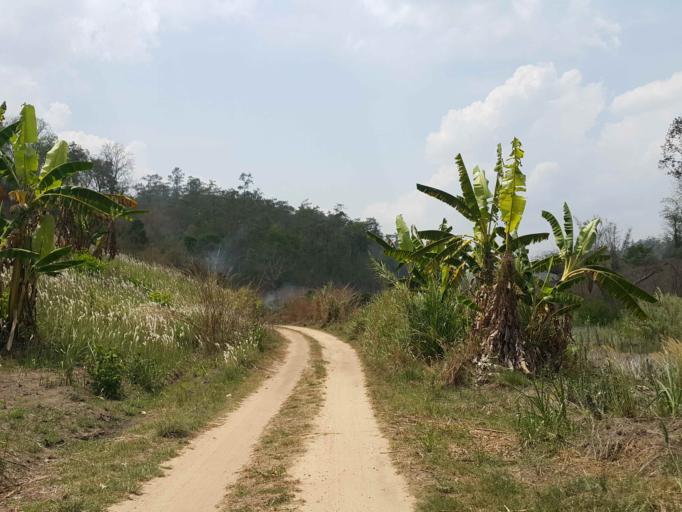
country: TH
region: Chiang Mai
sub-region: Amphoe Chiang Dao
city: Chiang Dao
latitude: 19.2789
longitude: 98.7651
